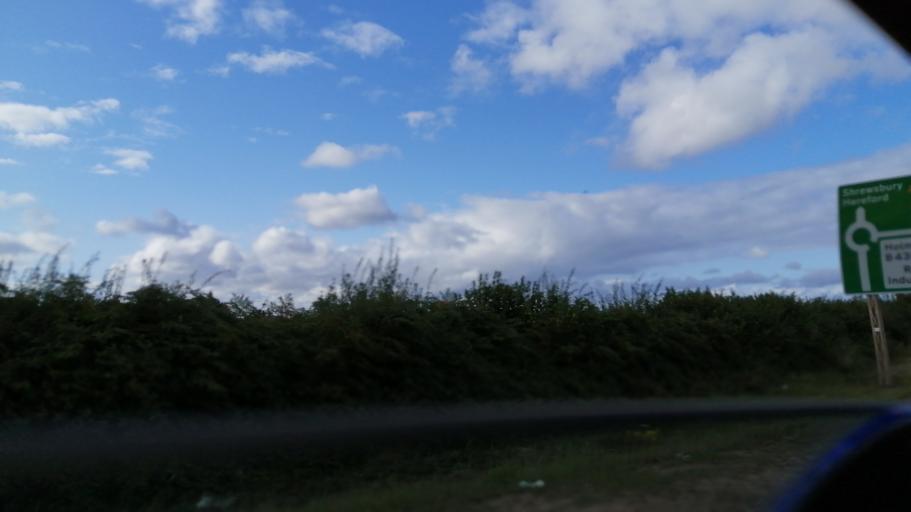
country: GB
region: England
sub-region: Herefordshire
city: Callow
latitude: 52.0237
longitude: -2.7246
